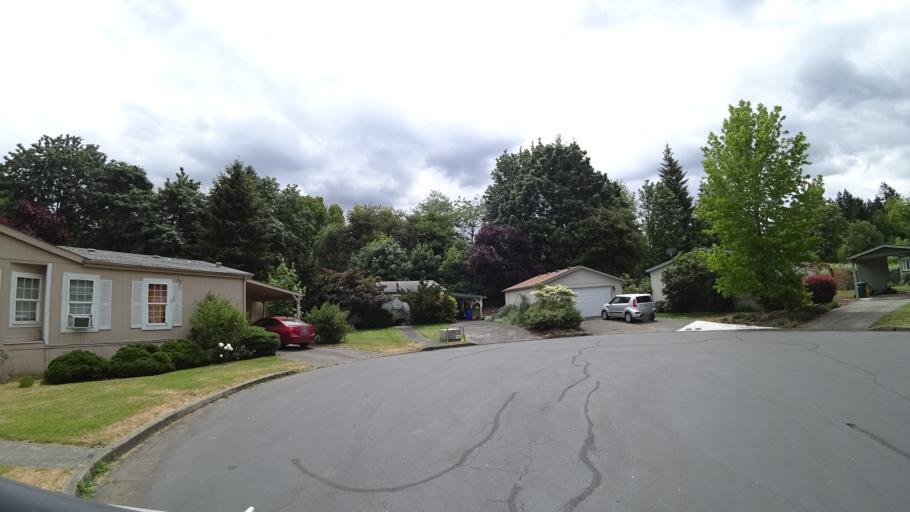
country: US
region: Oregon
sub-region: Clackamas County
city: Happy Valley
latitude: 45.4858
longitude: -122.5254
